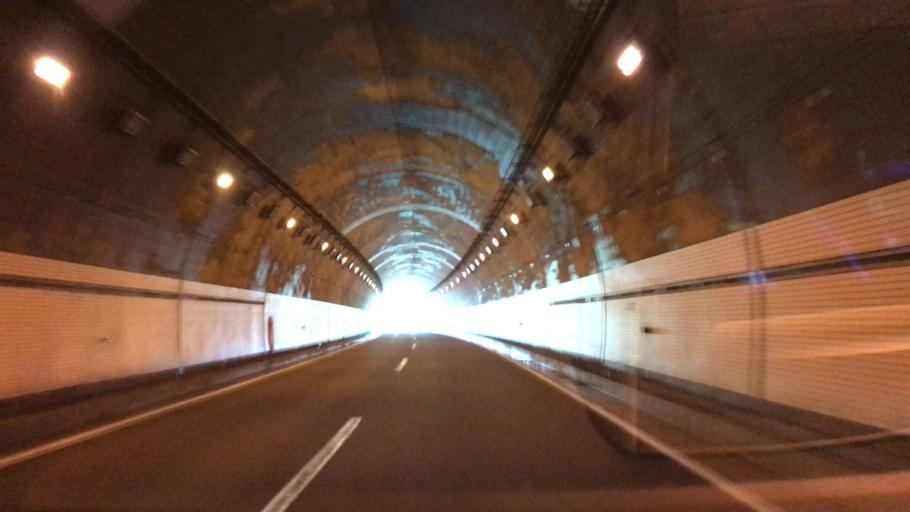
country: JP
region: Hokkaido
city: Shiraoi
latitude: 42.4742
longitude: 141.2156
